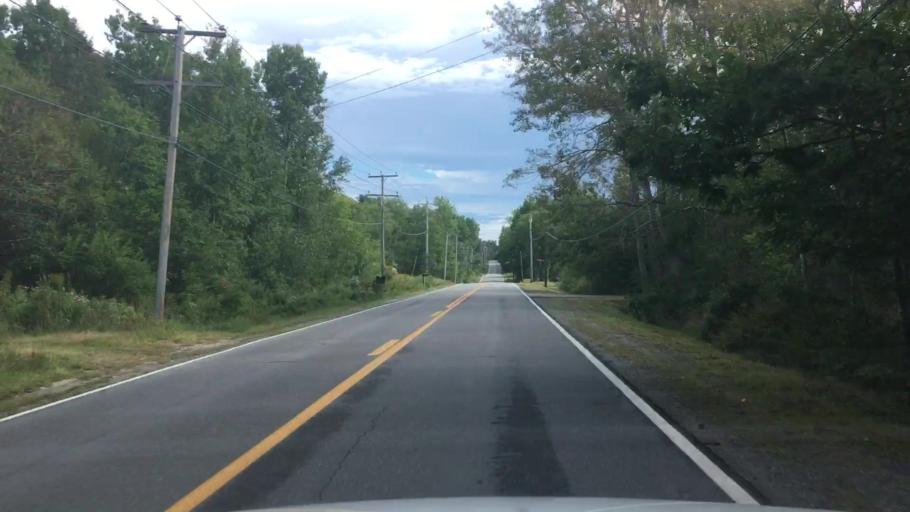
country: US
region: Maine
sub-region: Hancock County
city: Ellsworth
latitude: 44.4946
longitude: -68.4202
